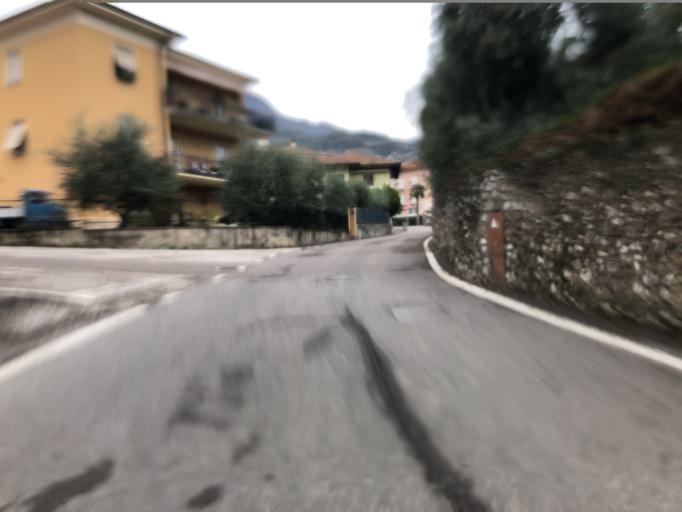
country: IT
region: Trentino-Alto Adige
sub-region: Provincia di Trento
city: Tenno
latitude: 45.9055
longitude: 10.8404
